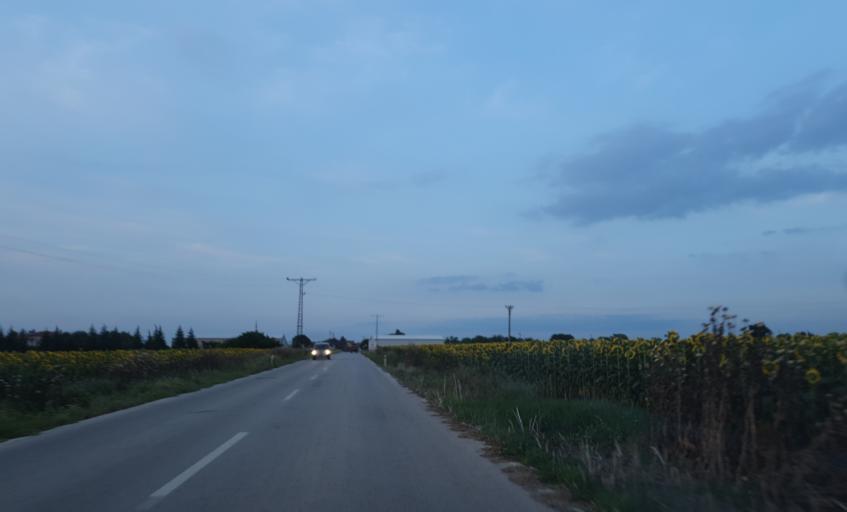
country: TR
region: Tekirdag
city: Beyazkoy
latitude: 41.4078
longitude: 27.6490
